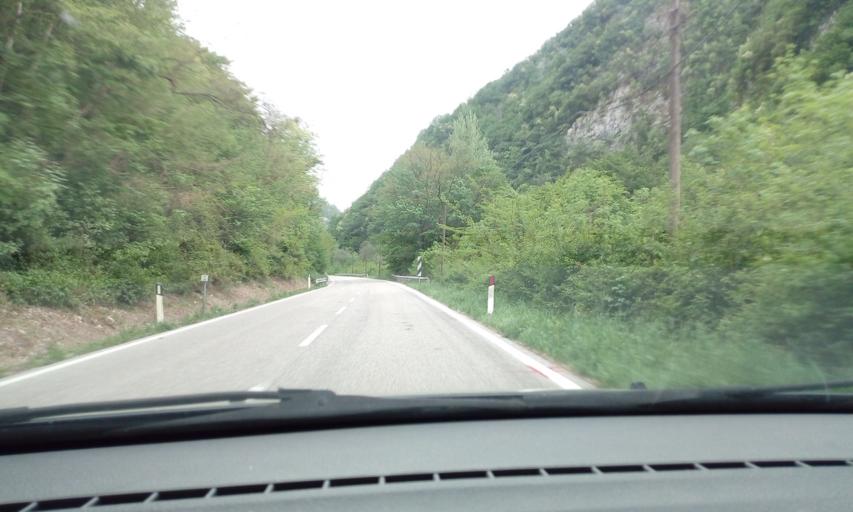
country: IT
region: Friuli Venezia Giulia
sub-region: Provincia di Udine
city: Pulfero
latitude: 46.1891
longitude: 13.4717
